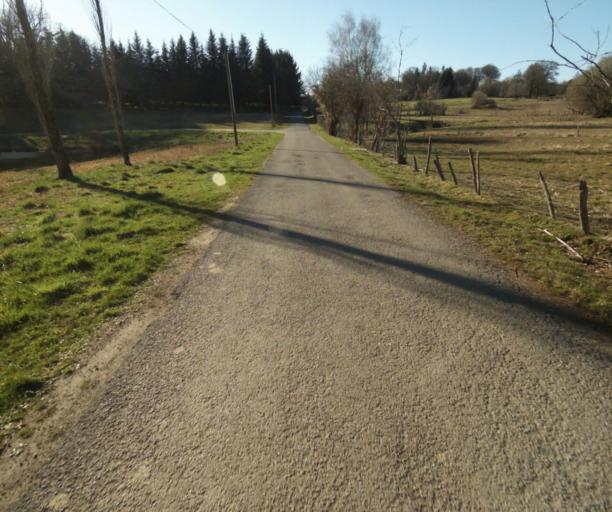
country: FR
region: Limousin
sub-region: Departement de la Correze
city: Seilhac
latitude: 45.3821
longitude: 1.7037
